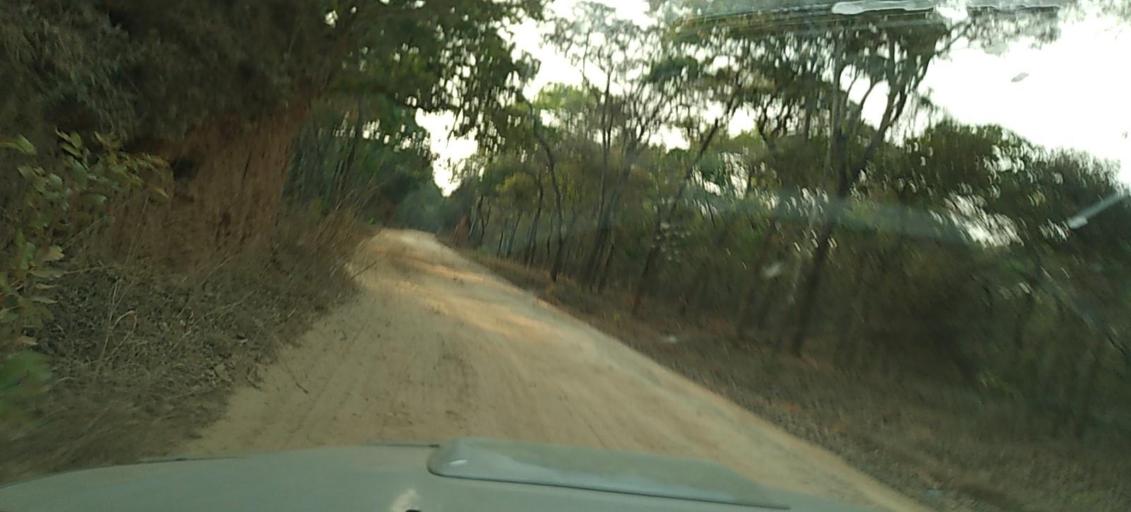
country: ZM
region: North-Western
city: Kasempa
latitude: -13.1609
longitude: 26.4512
